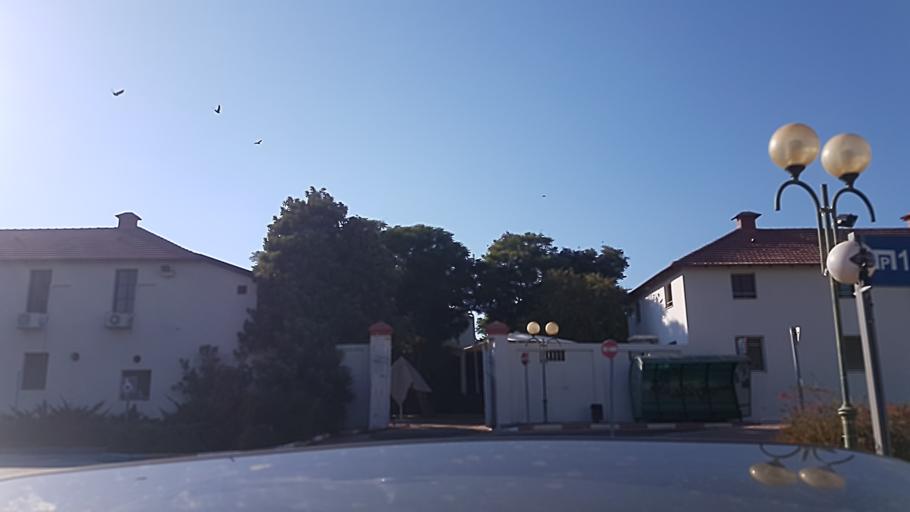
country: IL
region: Central District
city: Kfar Saba
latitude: 32.2008
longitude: 34.9191
